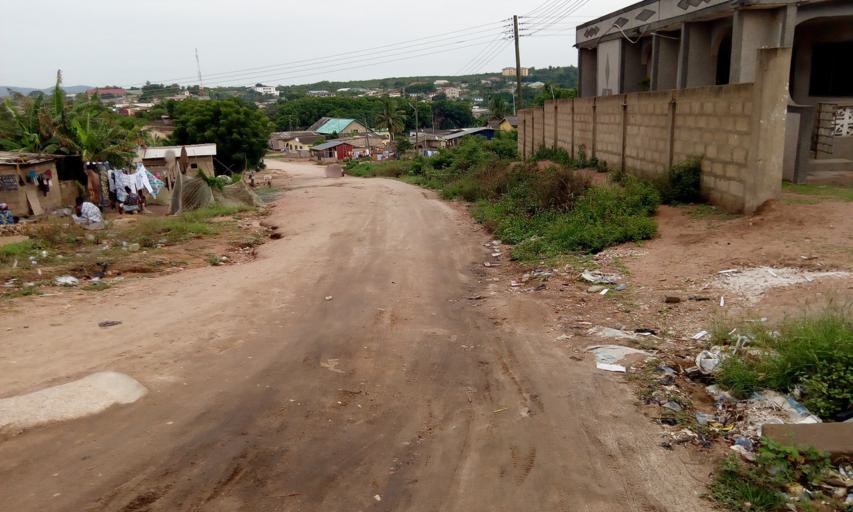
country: GH
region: Central
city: Winneba
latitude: 5.3553
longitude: -0.6161
